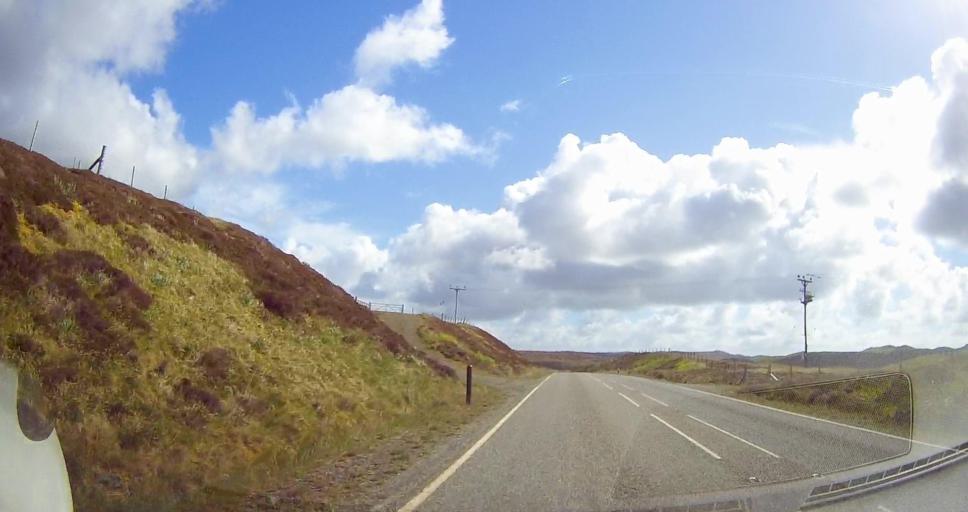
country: GB
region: Scotland
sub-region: Shetland Islands
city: Lerwick
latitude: 60.4703
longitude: -1.4068
